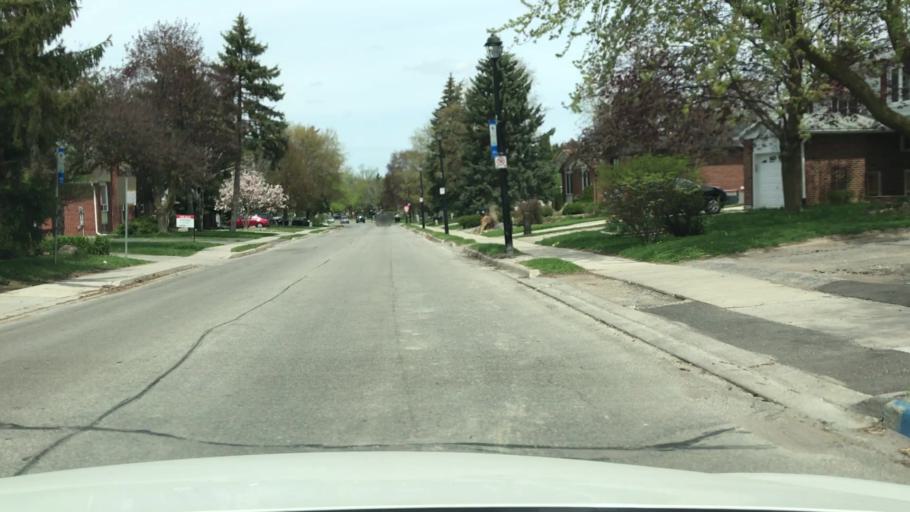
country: CA
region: Ontario
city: Newmarket
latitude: 44.0423
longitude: -79.4700
